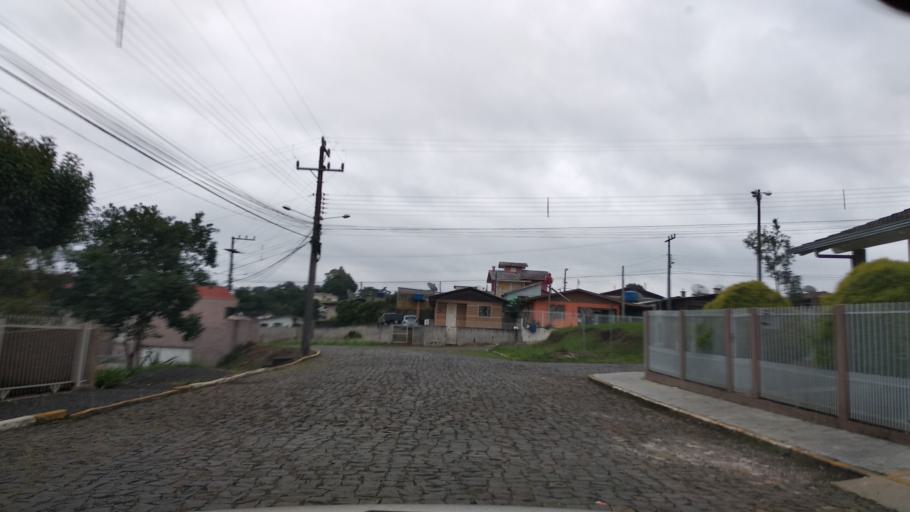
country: BR
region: Santa Catarina
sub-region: Videira
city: Videira
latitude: -26.9874
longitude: -51.1737
